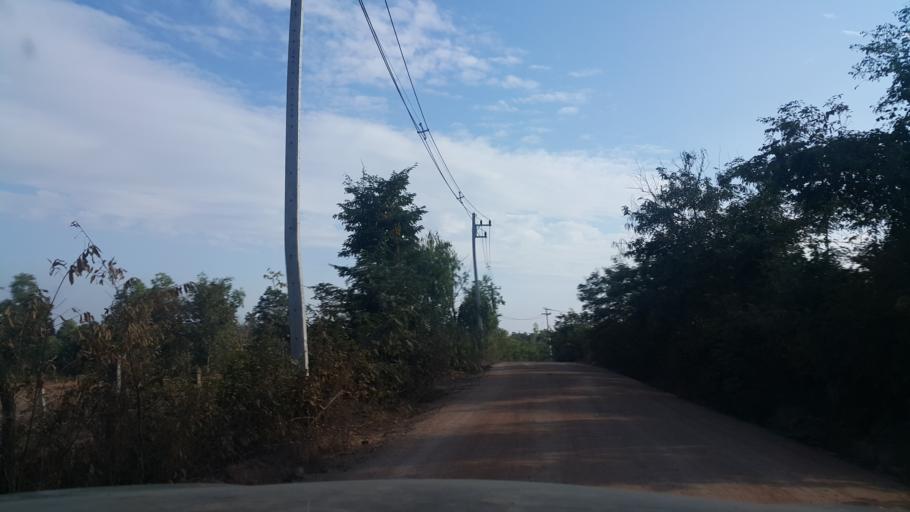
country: TH
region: Lampang
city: Hang Chat
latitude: 18.3011
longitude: 99.3524
